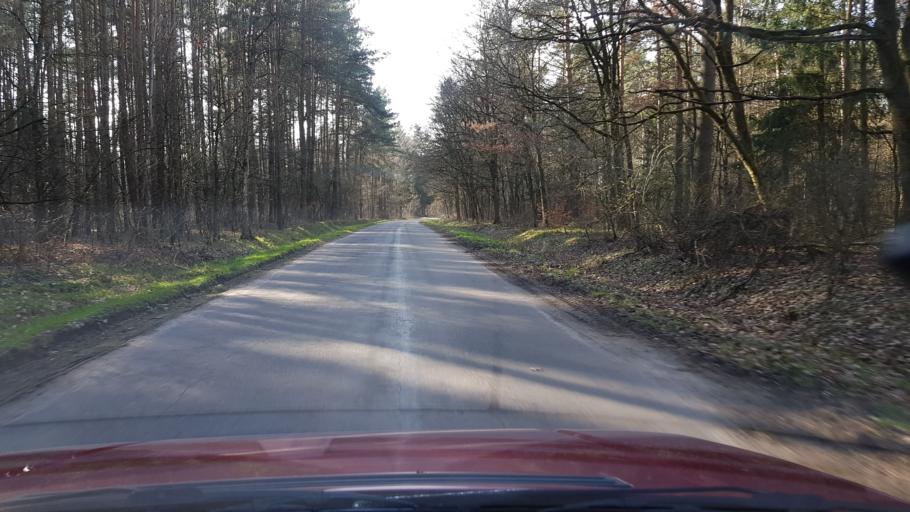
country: PL
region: West Pomeranian Voivodeship
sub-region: Powiat gryficki
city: Ploty
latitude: 53.8306
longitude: 15.3216
